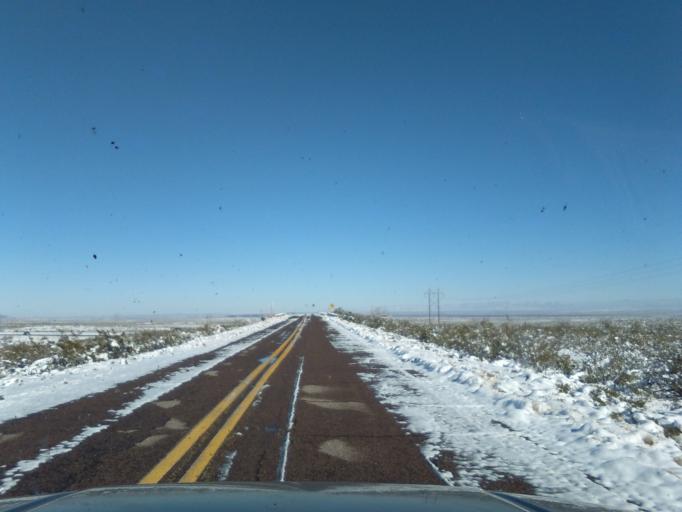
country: US
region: New Mexico
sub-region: Sierra County
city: Elephant Butte
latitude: 33.6062
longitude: -107.1547
